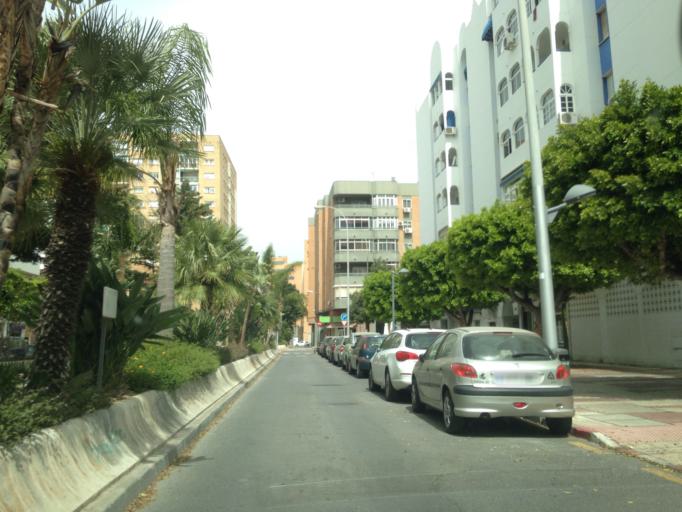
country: ES
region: Andalusia
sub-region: Provincia de Malaga
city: Malaga
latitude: 36.7087
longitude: -4.4318
